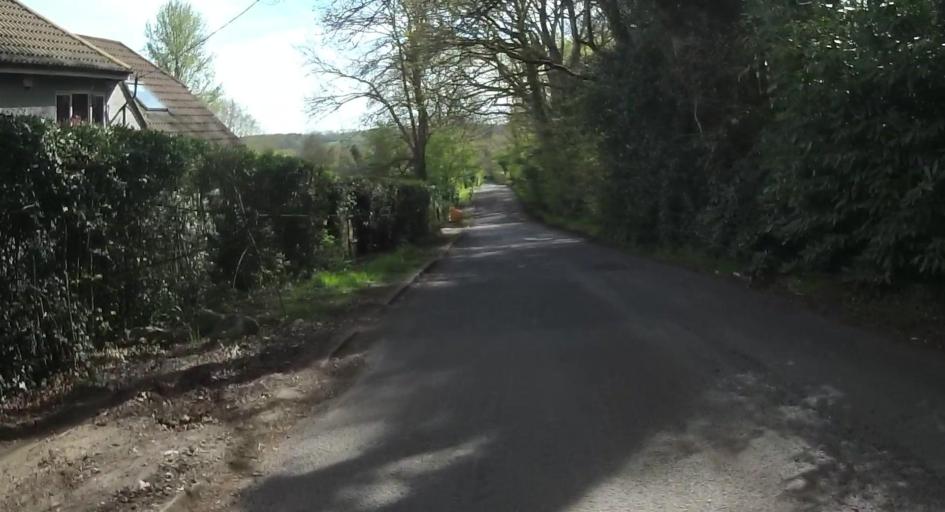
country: GB
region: England
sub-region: Surrey
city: Farnham
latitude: 51.1807
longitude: -0.8257
